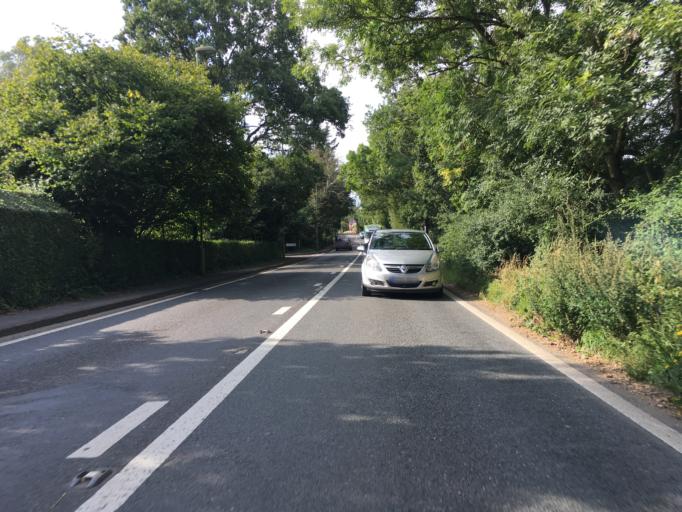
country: GB
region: England
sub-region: Hampshire
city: Colden Common
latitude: 50.9936
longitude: -1.3105
